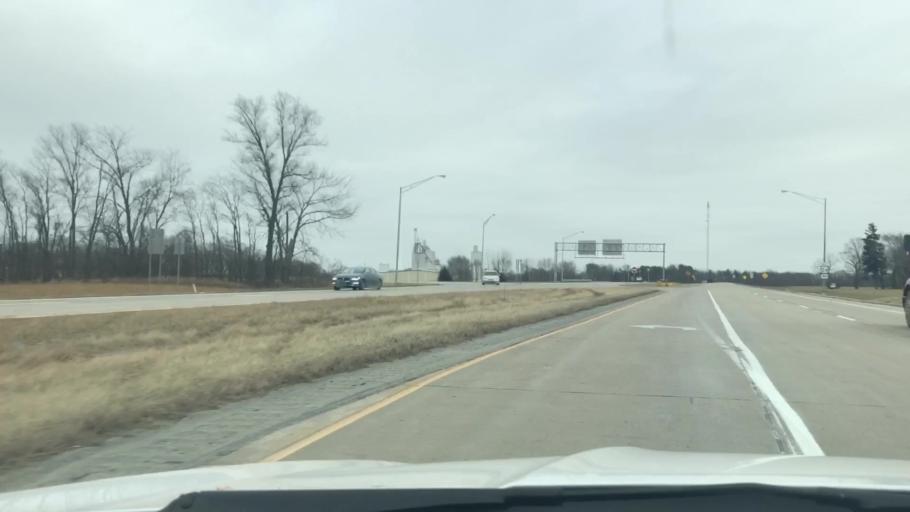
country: US
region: Indiana
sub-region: Cass County
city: Logansport
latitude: 40.7303
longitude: -86.3087
